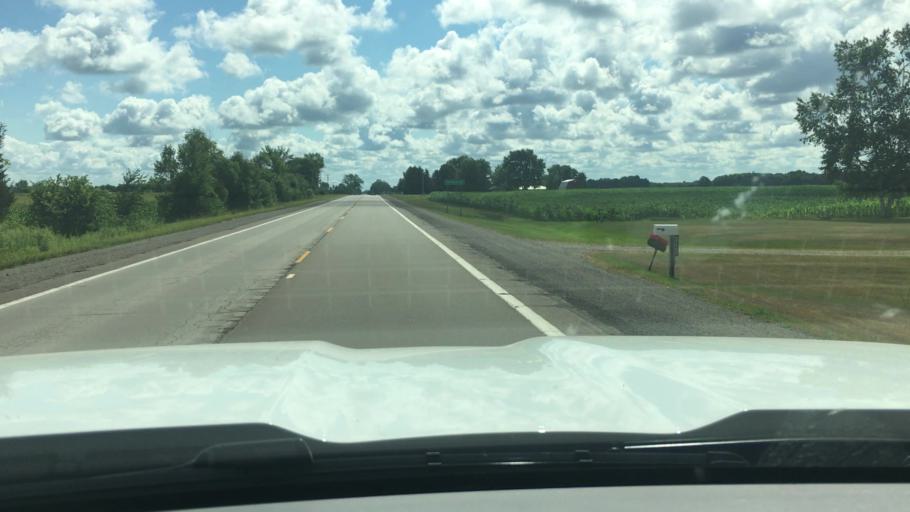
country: US
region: Michigan
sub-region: Shiawassee County
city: New Haven
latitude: 43.1869
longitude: -84.2514
